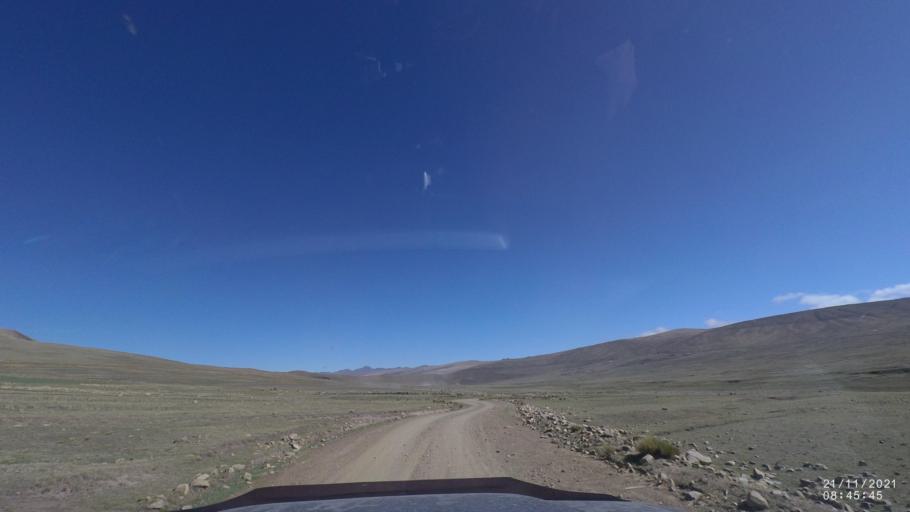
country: BO
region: Cochabamba
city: Cochabamba
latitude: -17.2466
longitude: -66.2323
